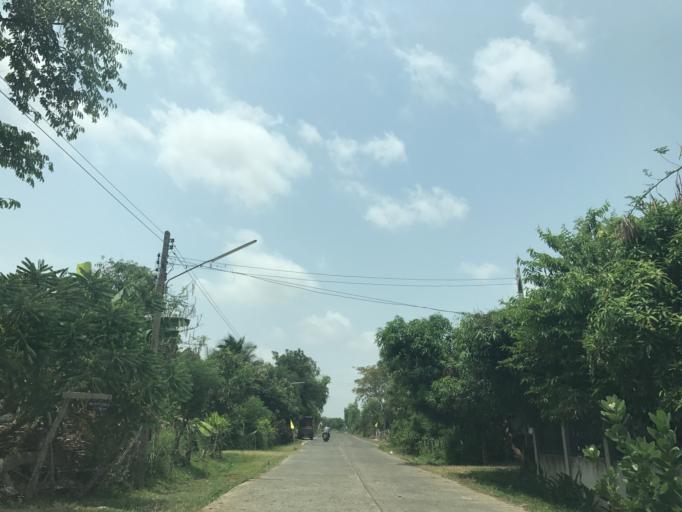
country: TH
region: Surin
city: Chom Phra
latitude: 15.0621
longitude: 103.6623
